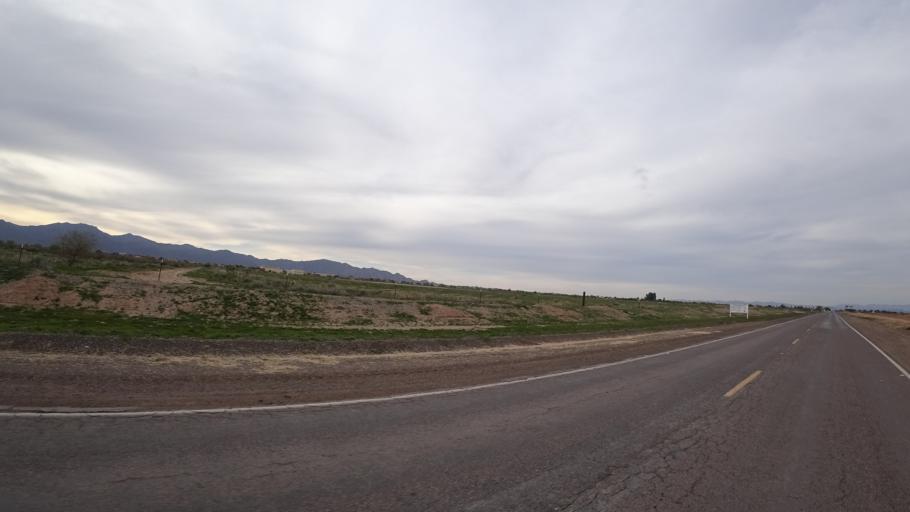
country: US
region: Arizona
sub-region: Maricopa County
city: Citrus Park
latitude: 33.5984
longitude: -112.4269
